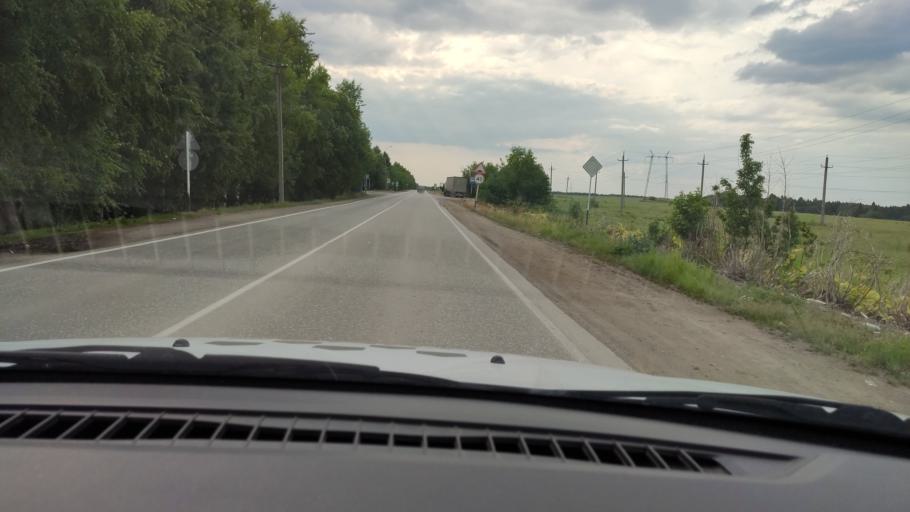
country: RU
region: Perm
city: Sylva
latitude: 58.0275
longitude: 56.7176
